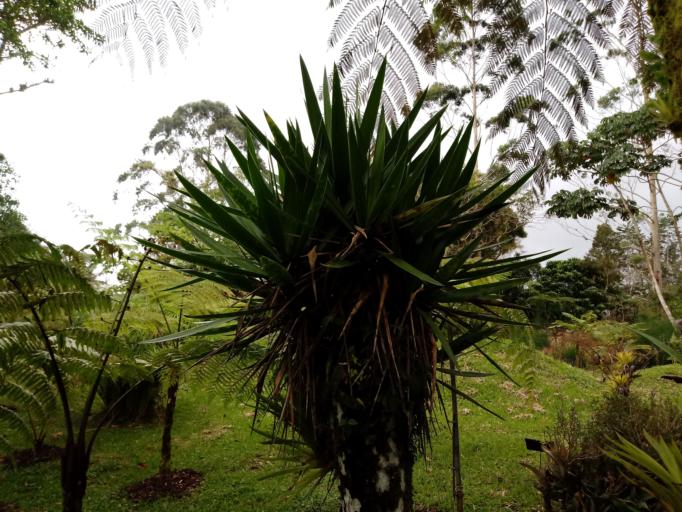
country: CR
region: Cartago
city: Paraiso
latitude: 9.8383
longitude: -83.8911
